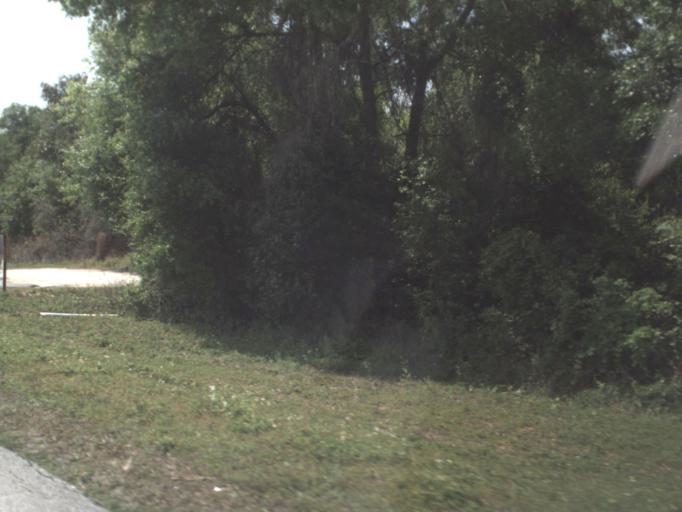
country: US
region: Florida
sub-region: Lake County
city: Astor
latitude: 29.2777
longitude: -81.6477
